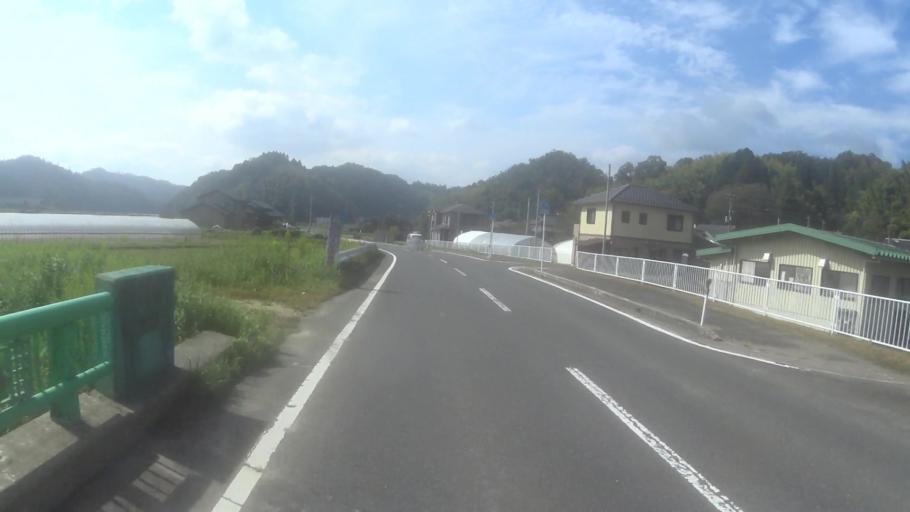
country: JP
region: Kyoto
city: Miyazu
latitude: 35.5949
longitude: 135.1341
